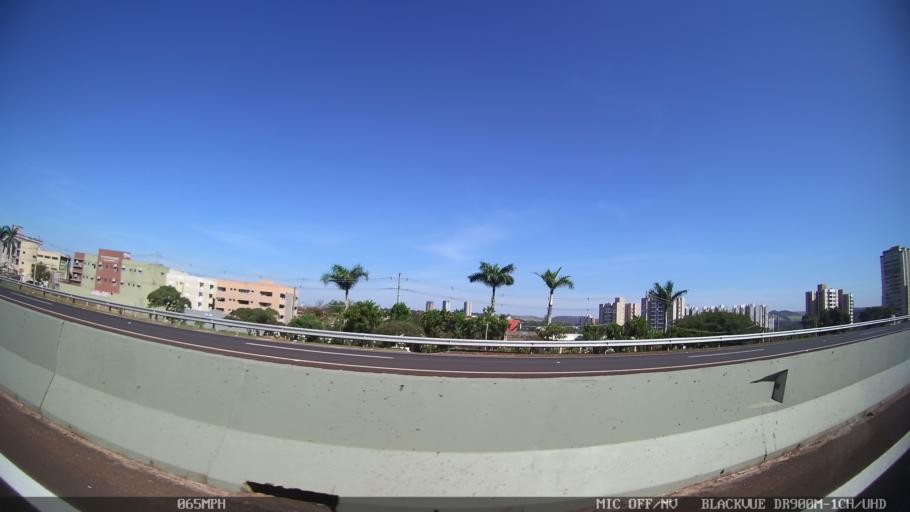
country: BR
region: Sao Paulo
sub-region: Ribeirao Preto
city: Ribeirao Preto
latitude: -21.2202
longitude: -47.8261
